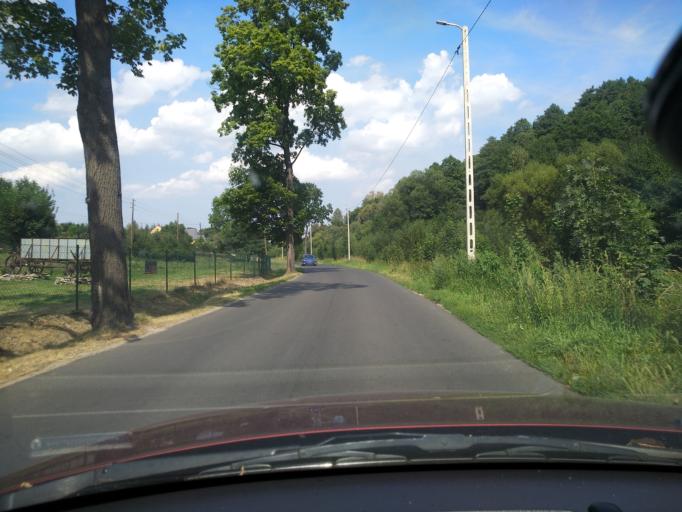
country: PL
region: Lower Silesian Voivodeship
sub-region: Powiat jeleniogorski
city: Stara Kamienica
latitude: 50.9057
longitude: 15.5689
